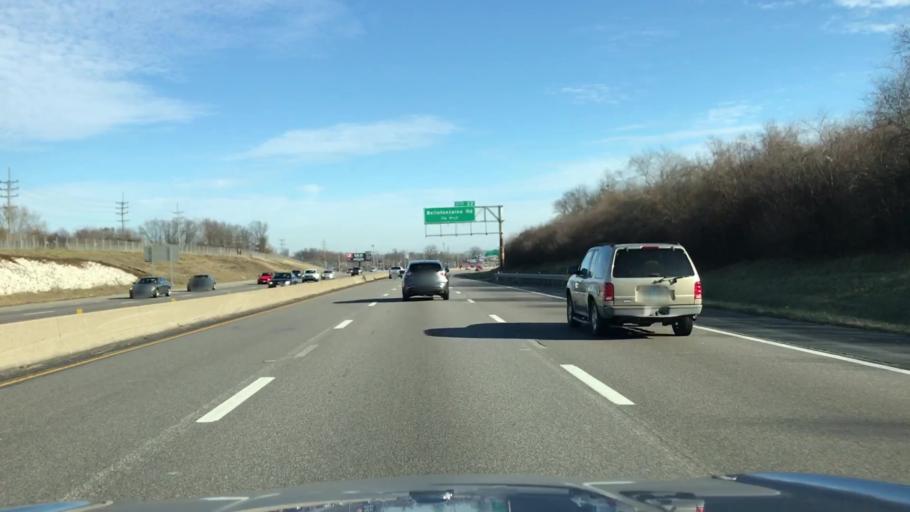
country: US
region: Missouri
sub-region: Saint Louis County
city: Spanish Lake
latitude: 38.7706
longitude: -90.2286
